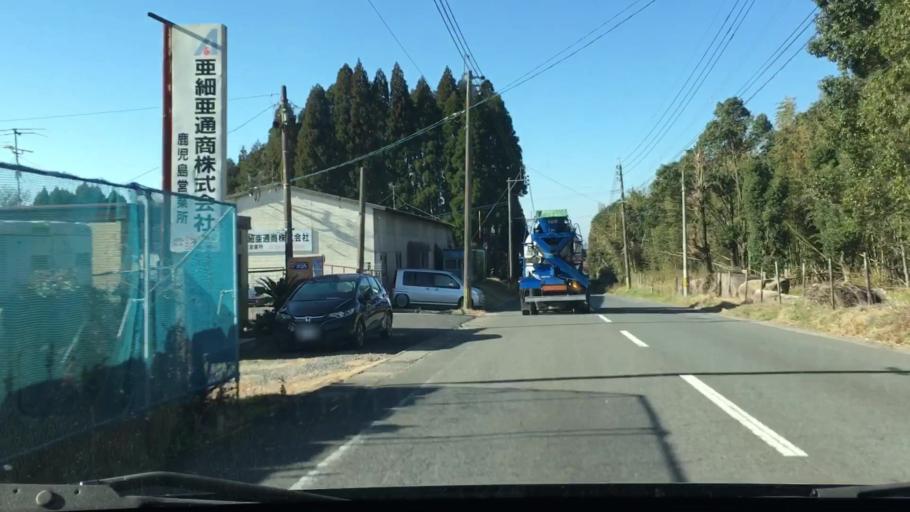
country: JP
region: Kagoshima
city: Kajiki
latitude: 31.7727
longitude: 130.6983
